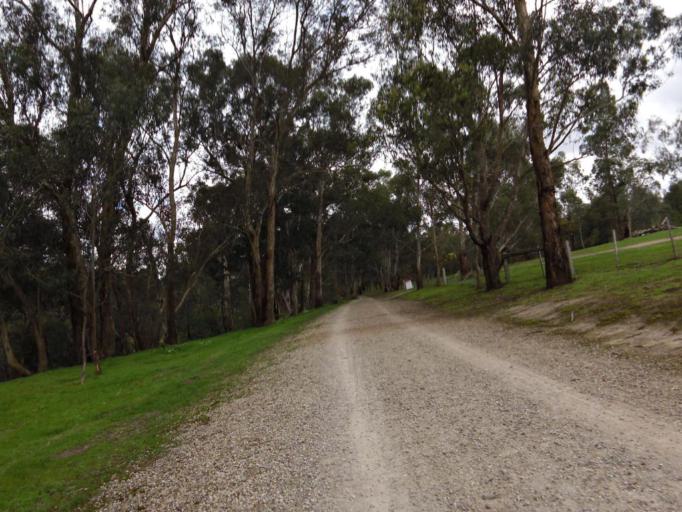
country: AU
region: Victoria
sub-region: Nillumbik
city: Eltham
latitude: -37.7352
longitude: 145.1569
